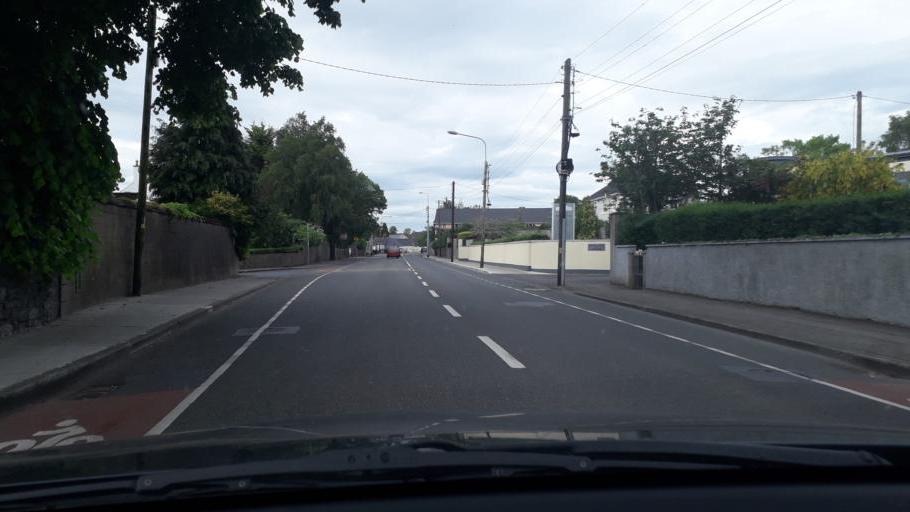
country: IE
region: Leinster
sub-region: County Carlow
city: Carlow
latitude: 52.8318
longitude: -6.9344
